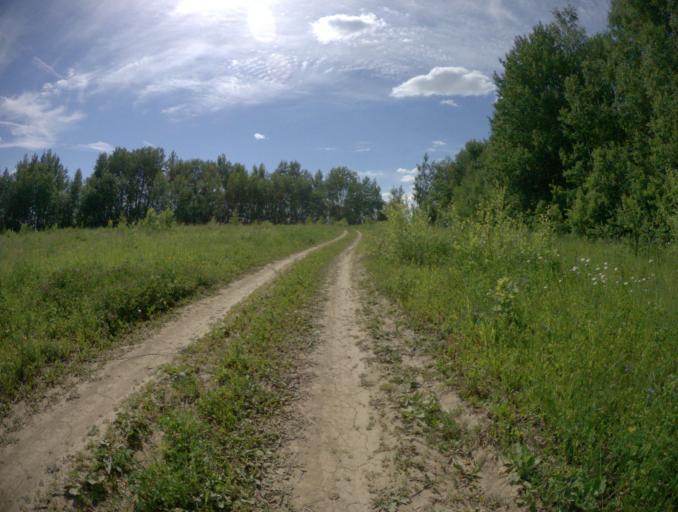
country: RU
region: Vladimir
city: Stavrovo
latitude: 56.3032
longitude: 40.0705
